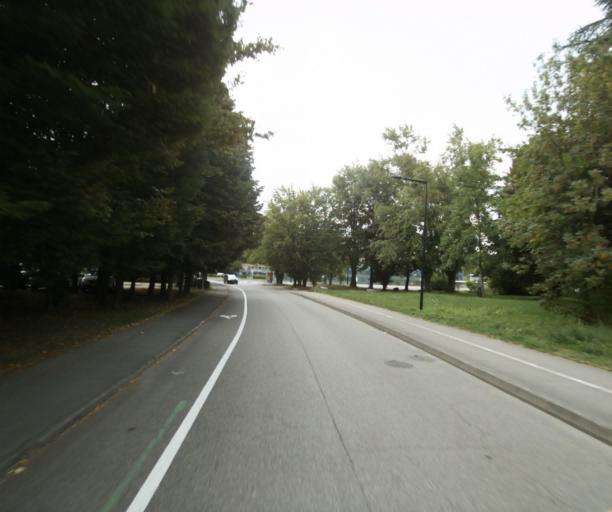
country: FR
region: Rhone-Alpes
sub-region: Departement de l'Isere
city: Gieres
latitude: 45.1911
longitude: 5.7758
